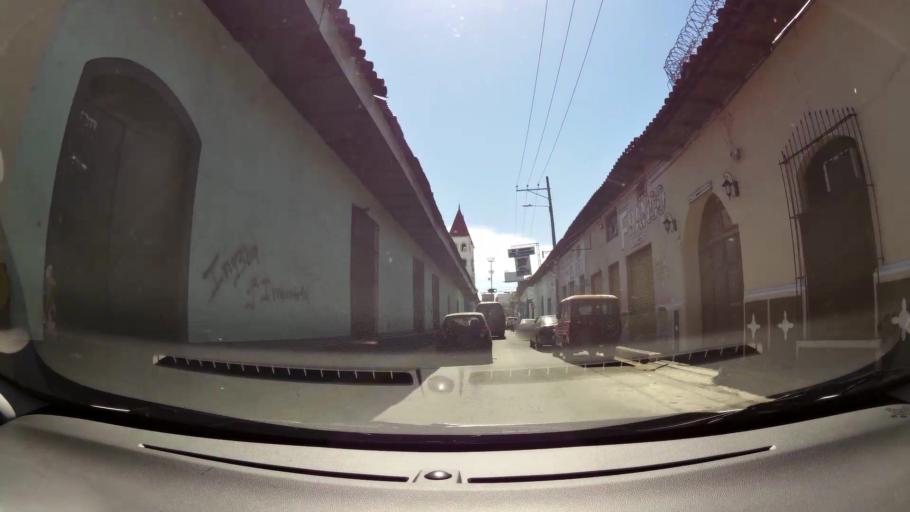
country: SV
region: San Miguel
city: San Miguel
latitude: 13.4848
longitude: -88.1752
